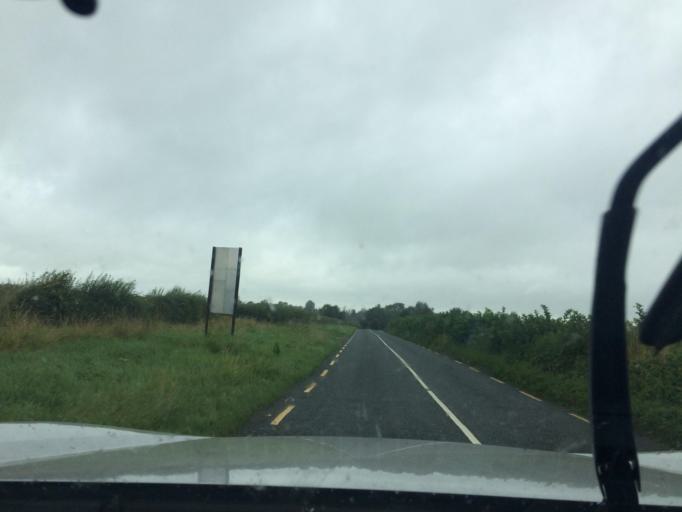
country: IE
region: Munster
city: Cashel
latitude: 52.5305
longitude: -7.8896
